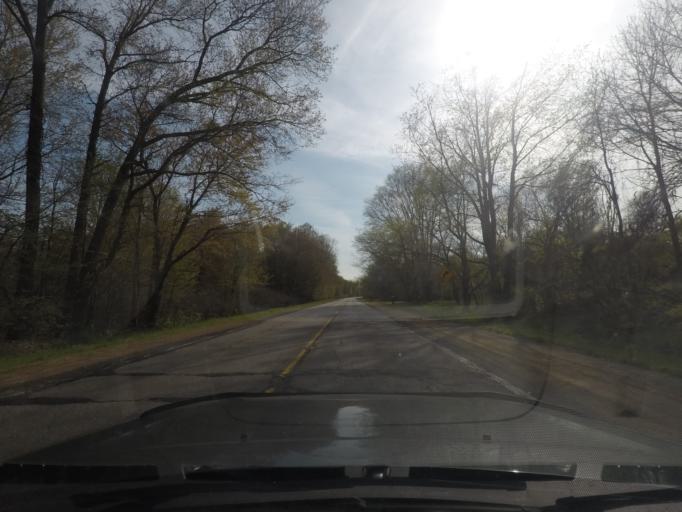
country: US
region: Michigan
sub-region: Berrien County
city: Buchanan
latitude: 41.7959
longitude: -86.4166
